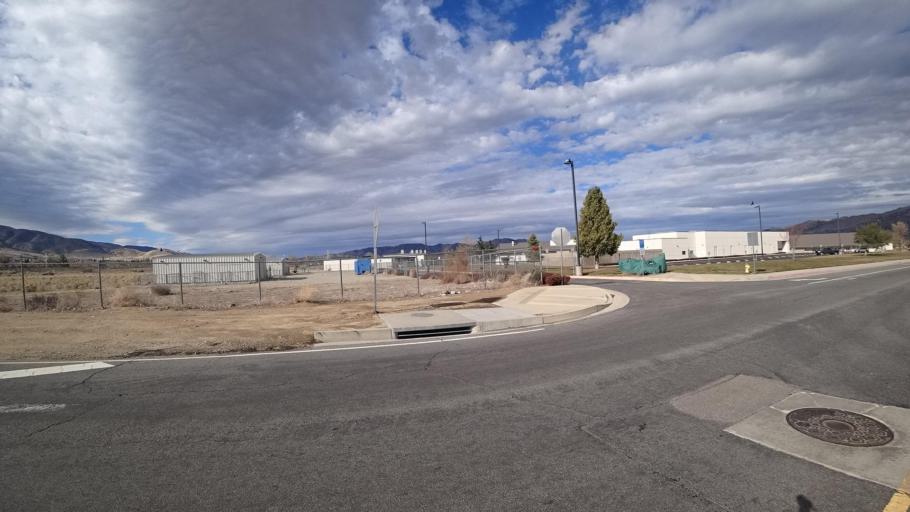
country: US
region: California
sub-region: Kern County
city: Tehachapi
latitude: 35.1193
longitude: -118.4324
